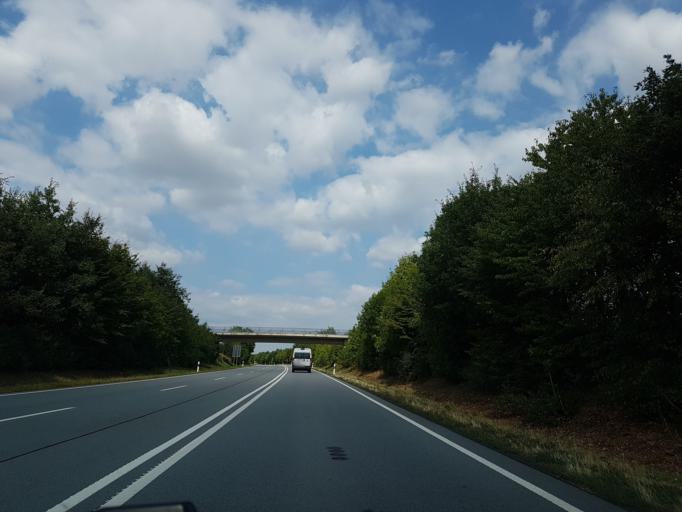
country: DE
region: Saxony
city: Zittau
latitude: 50.9241
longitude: 14.8141
